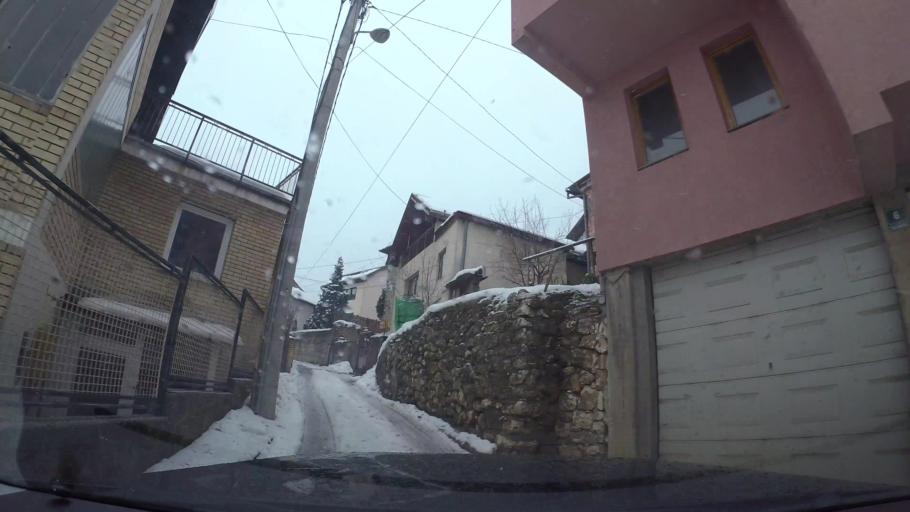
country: BA
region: Federation of Bosnia and Herzegovina
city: Kobilja Glava
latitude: 43.8515
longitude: 18.4346
